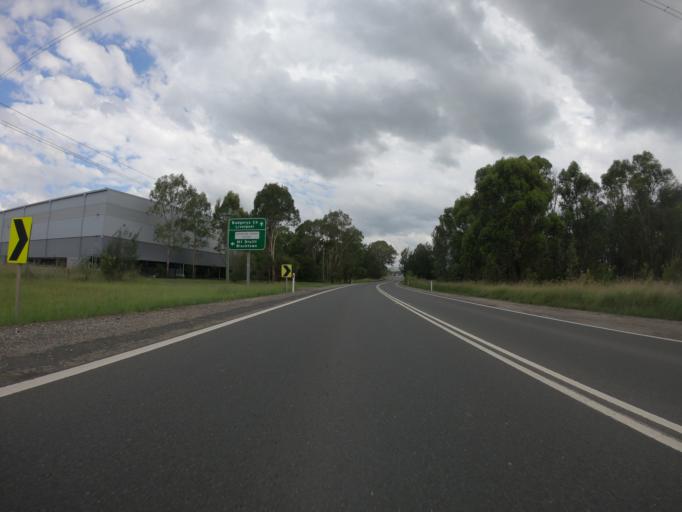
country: AU
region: New South Wales
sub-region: Blacktown
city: Mount Druitt
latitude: -33.8127
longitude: 150.7758
